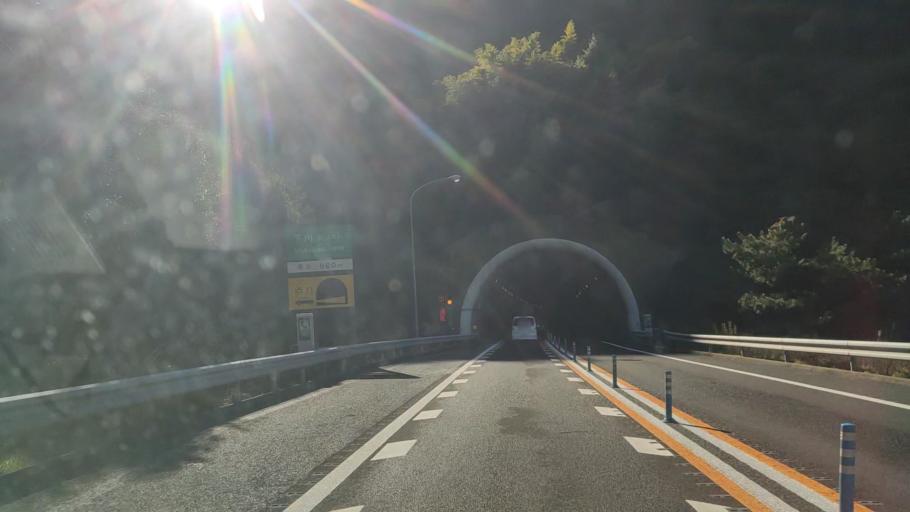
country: JP
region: Ehime
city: Kawanoecho
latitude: 33.9990
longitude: 133.6412
